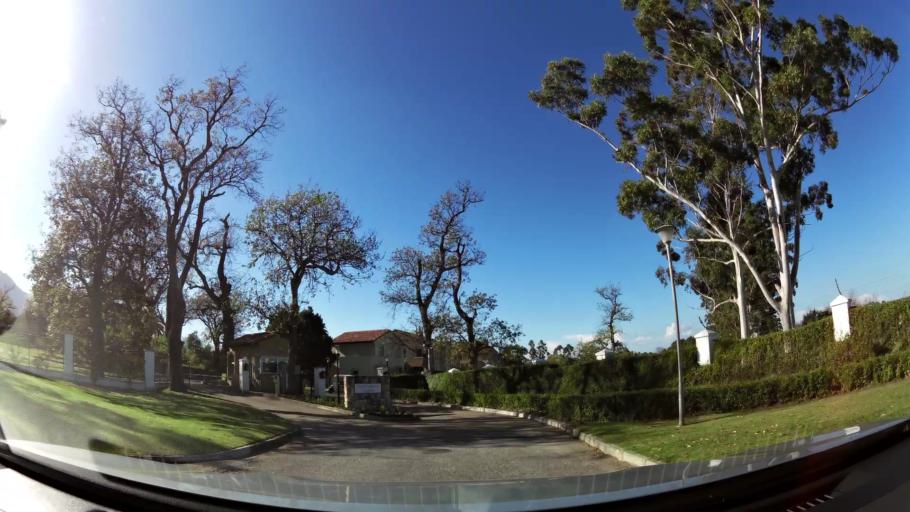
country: ZA
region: Western Cape
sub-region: Eden District Municipality
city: George
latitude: -33.9502
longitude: 22.4181
